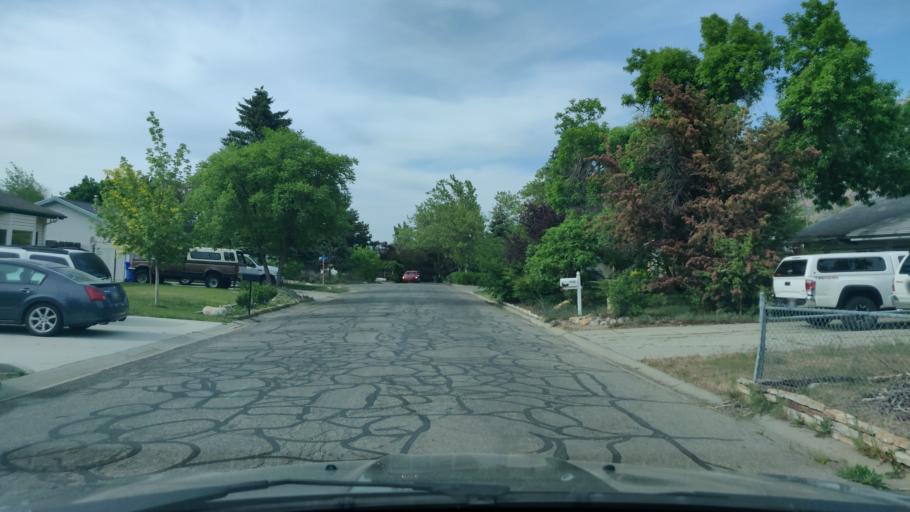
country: US
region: Utah
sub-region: Salt Lake County
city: Cottonwood Heights
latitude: 40.6191
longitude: -111.8087
